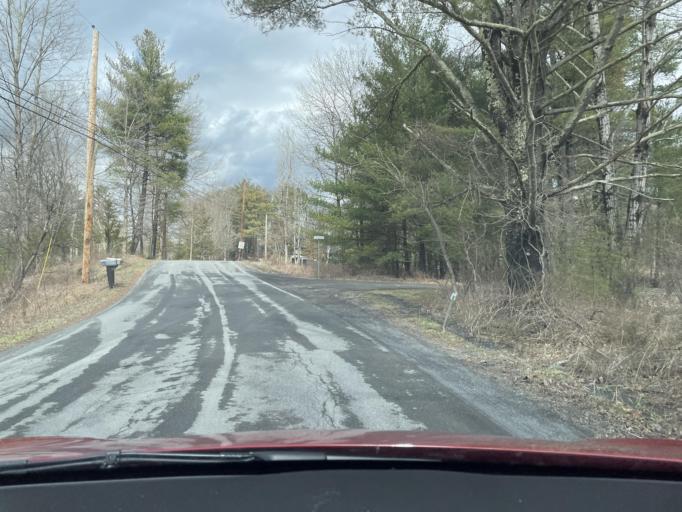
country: US
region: New York
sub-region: Ulster County
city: Zena
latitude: 42.0187
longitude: -74.0746
